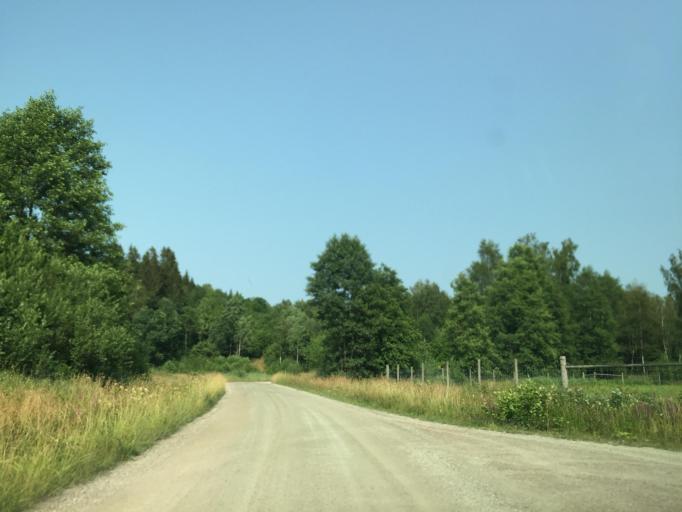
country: SE
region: Vaestra Goetaland
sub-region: Trollhattan
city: Sjuntorp
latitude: 58.2734
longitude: 12.1081
